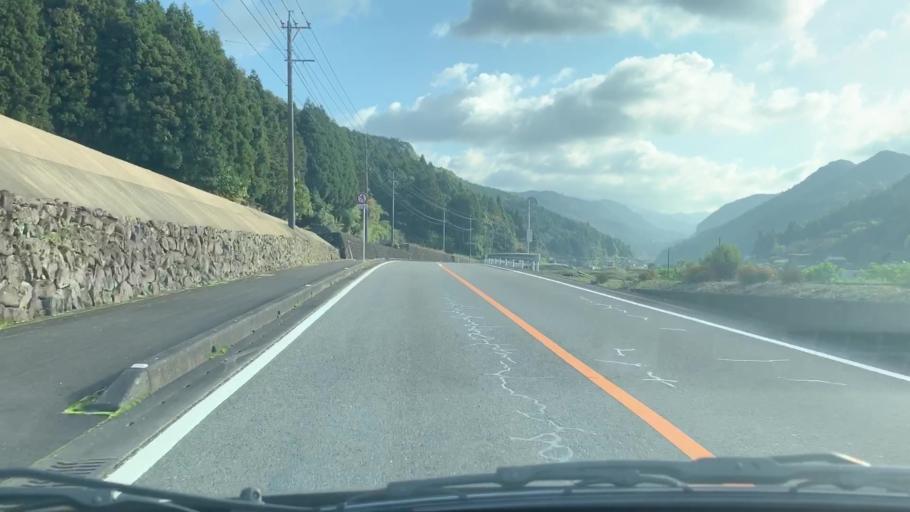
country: JP
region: Saga Prefecture
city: Kashima
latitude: 33.0700
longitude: 130.0697
